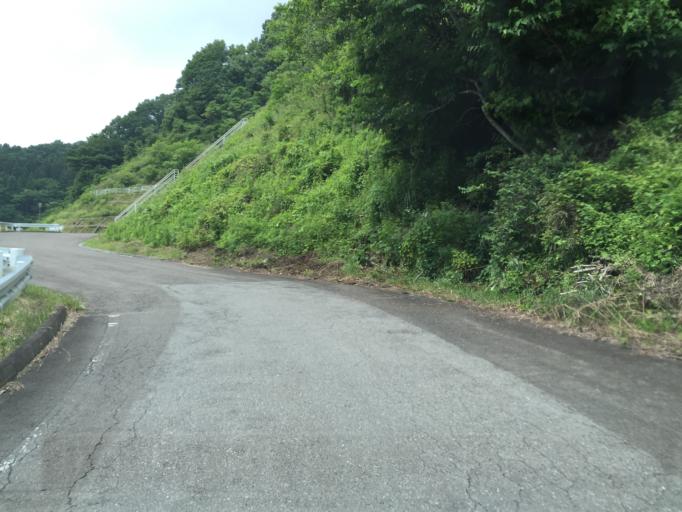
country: JP
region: Miyagi
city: Marumori
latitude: 37.7974
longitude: 140.7741
